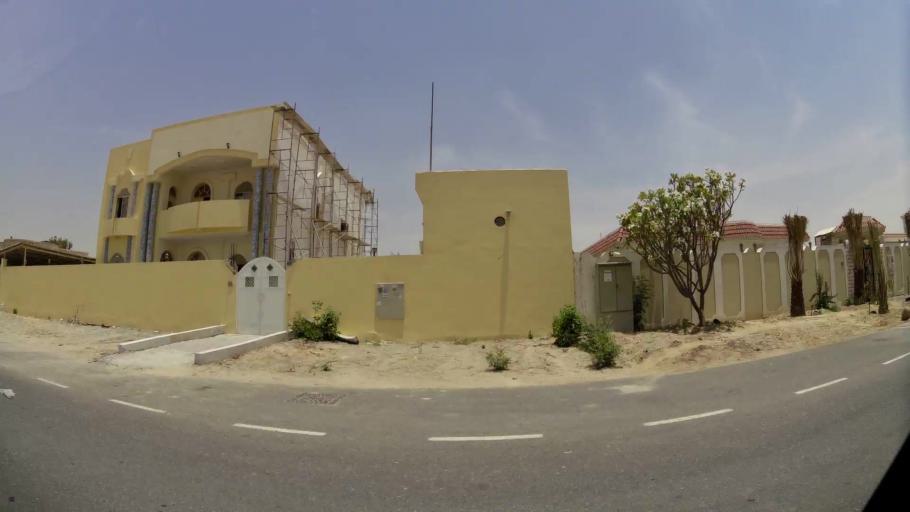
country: AE
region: Ash Shariqah
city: Sharjah
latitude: 25.2090
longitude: 55.3953
